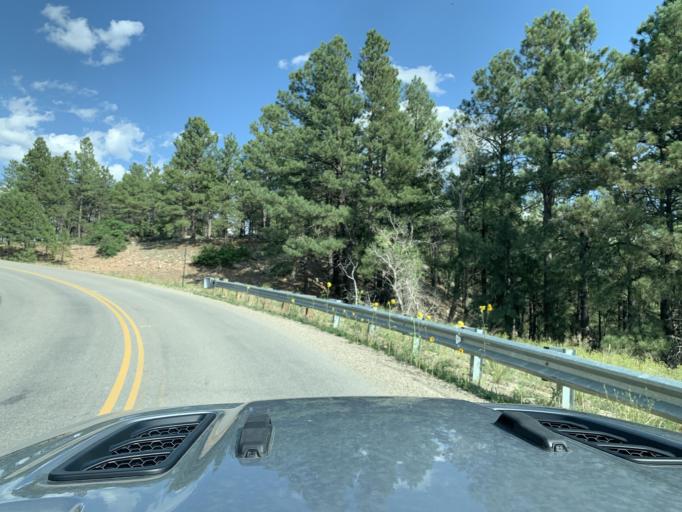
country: US
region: Colorado
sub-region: Archuleta County
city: Pagosa Springs
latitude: 37.2402
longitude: -107.0262
